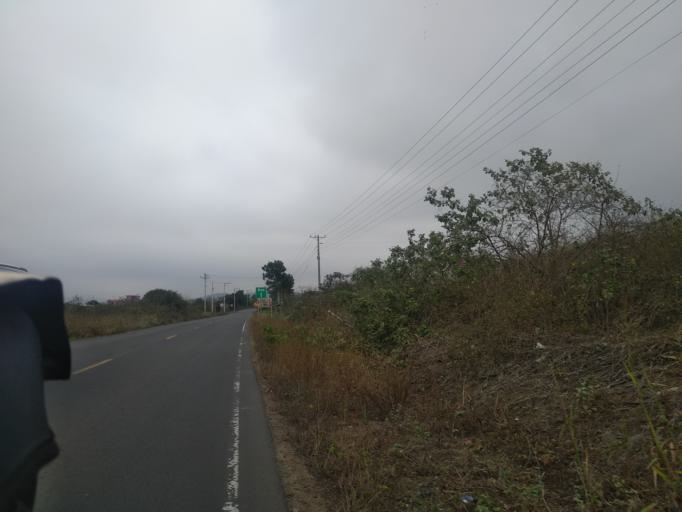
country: EC
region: Manabi
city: Montecristi
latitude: -1.0680
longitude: -80.6593
